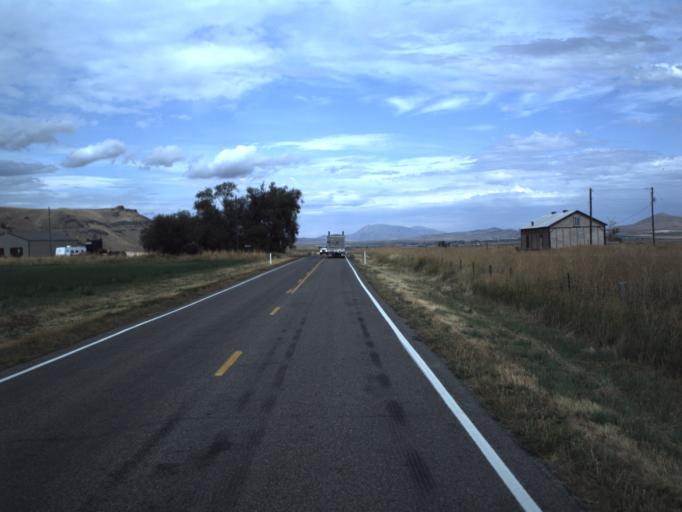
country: US
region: Utah
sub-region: Cache County
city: Benson
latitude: 41.7669
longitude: -111.9810
